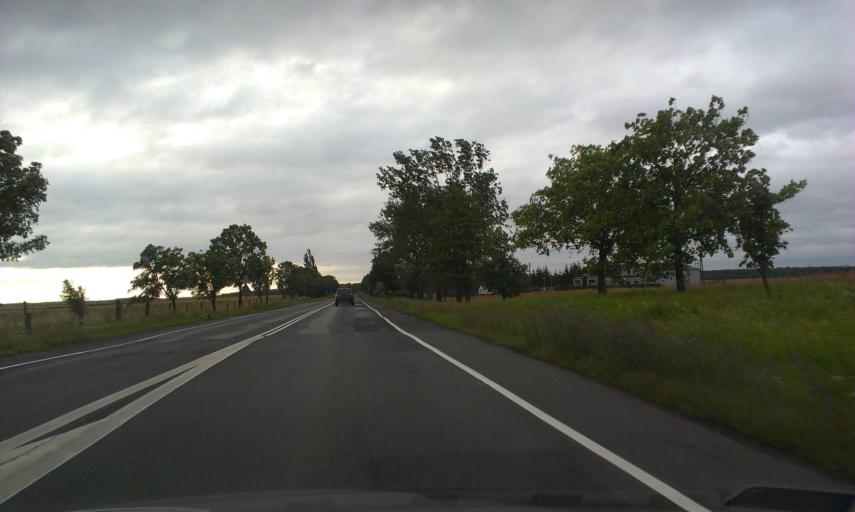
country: PL
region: Greater Poland Voivodeship
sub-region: Powiat pilski
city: Ujscie
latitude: 53.0387
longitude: 16.7695
